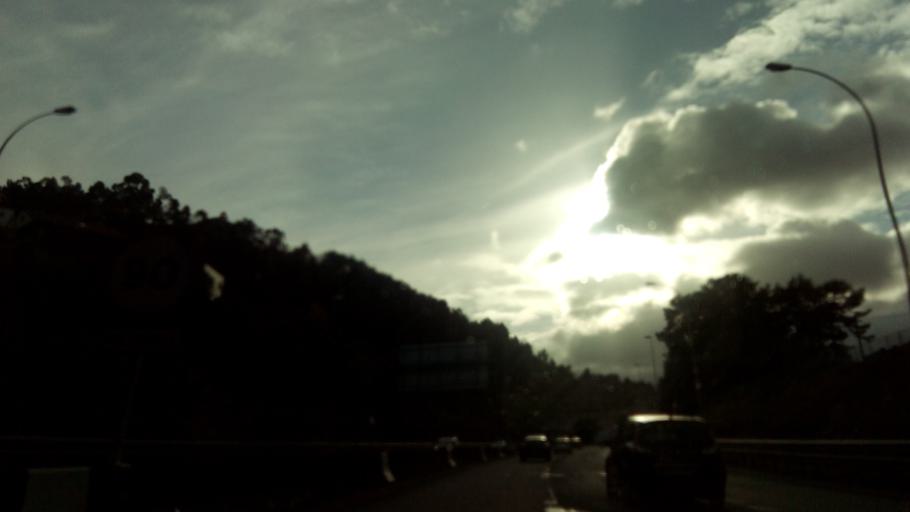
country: ES
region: Galicia
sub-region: Provincia de Pontevedra
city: Vigo
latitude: 42.2562
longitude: -8.6758
